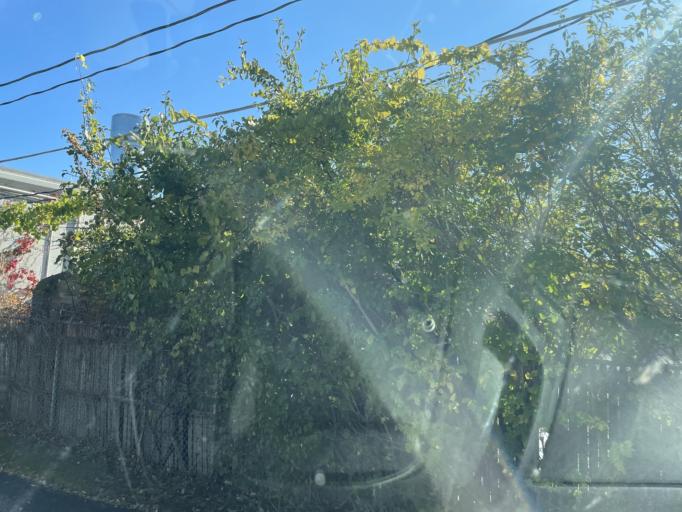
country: US
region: Wisconsin
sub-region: Waukesha County
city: Butler
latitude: 43.1145
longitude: -88.0566
